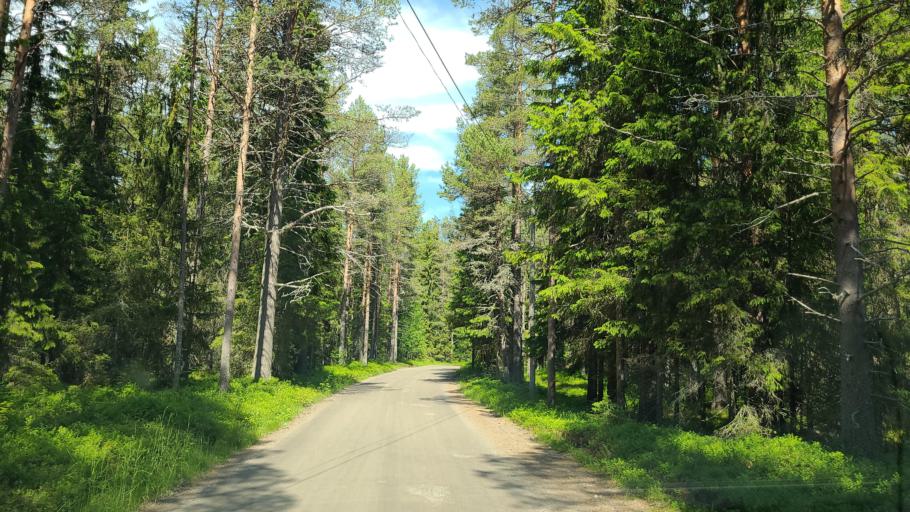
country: SE
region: Vaesterbotten
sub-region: Robertsfors Kommun
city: Robertsfors
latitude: 64.1413
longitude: 20.9607
